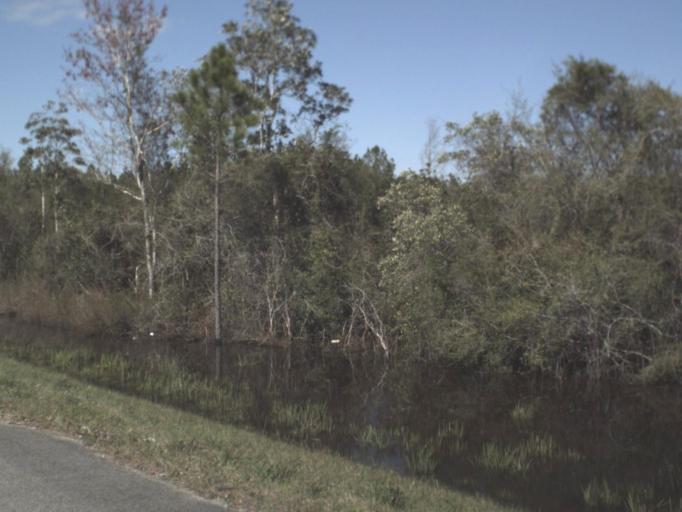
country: US
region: Florida
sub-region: Gulf County
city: Wewahitchka
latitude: 29.9865
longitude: -85.1683
